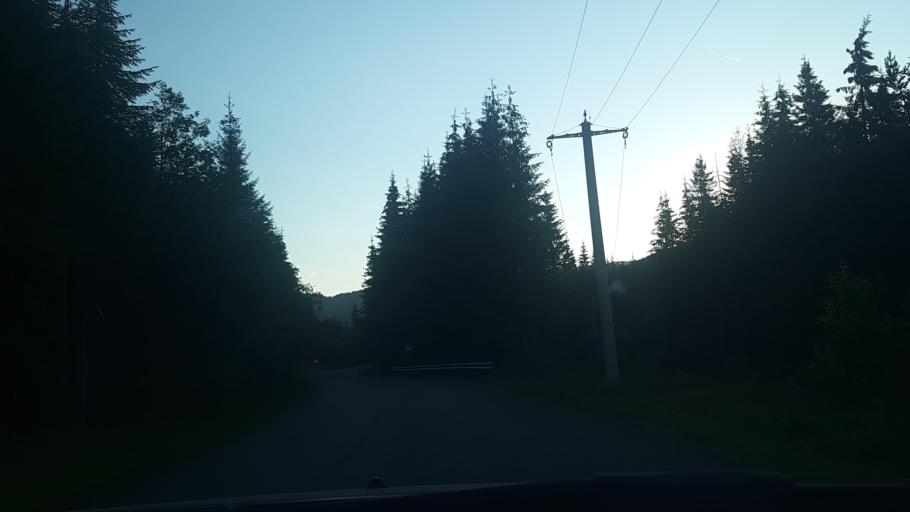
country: RO
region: Gorj
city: Novaci-Straini
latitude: 45.4311
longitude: 23.6702
